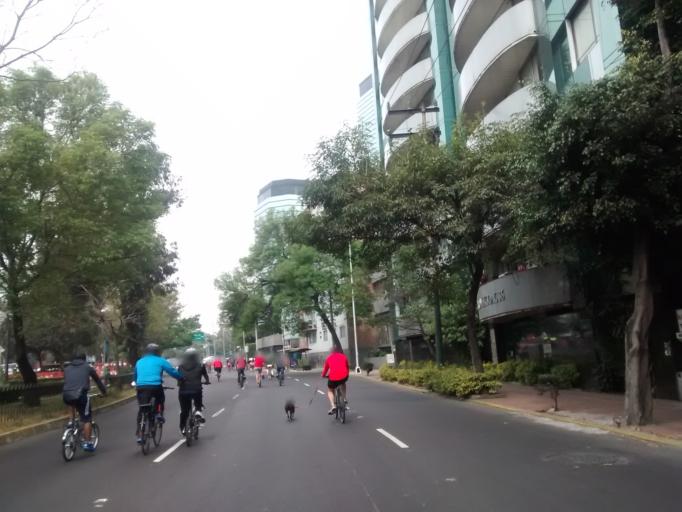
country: MX
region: Mexico City
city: Alvaro Obregon
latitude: 19.3671
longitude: -99.1794
